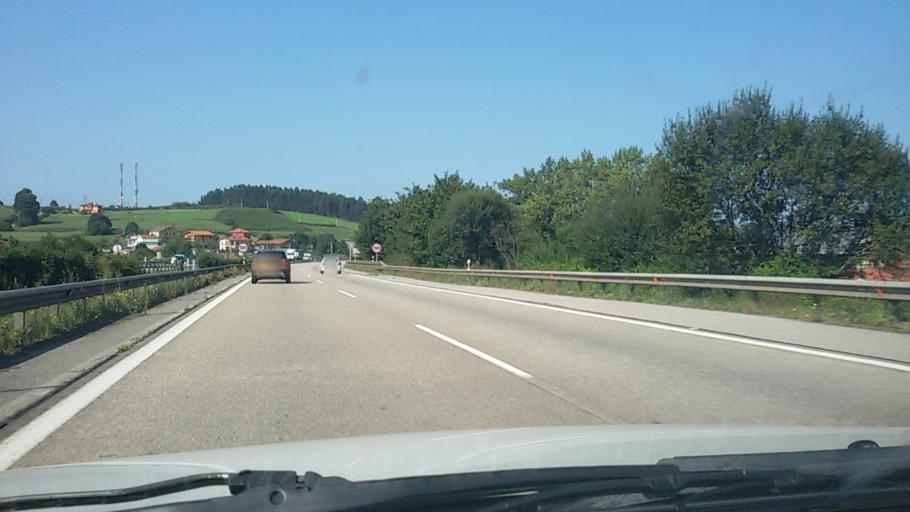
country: ES
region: Asturias
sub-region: Province of Asturias
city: Corvera de Asturias
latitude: 43.5505
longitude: -5.8755
